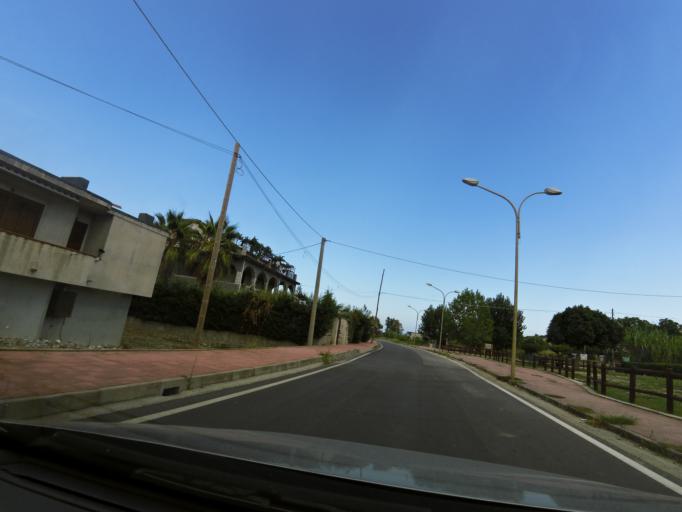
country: IT
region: Calabria
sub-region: Provincia di Reggio Calabria
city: Monasterace Marina
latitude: 38.4228
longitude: 16.5435
